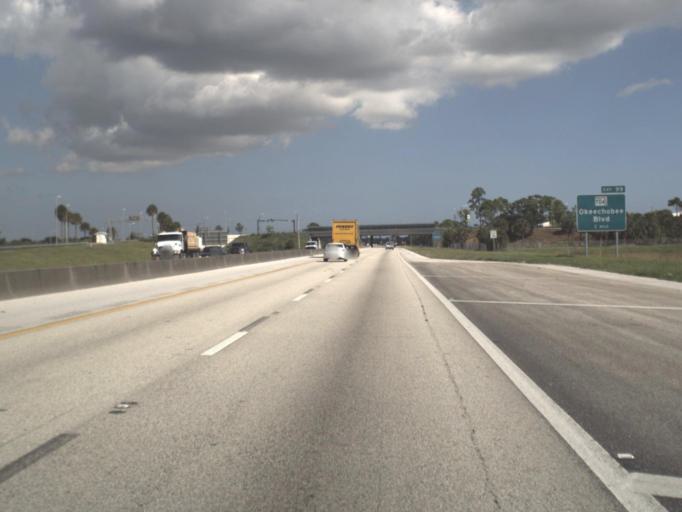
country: US
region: Florida
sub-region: Palm Beach County
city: Plantation Mobile Home Park
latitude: 26.6982
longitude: -80.1501
